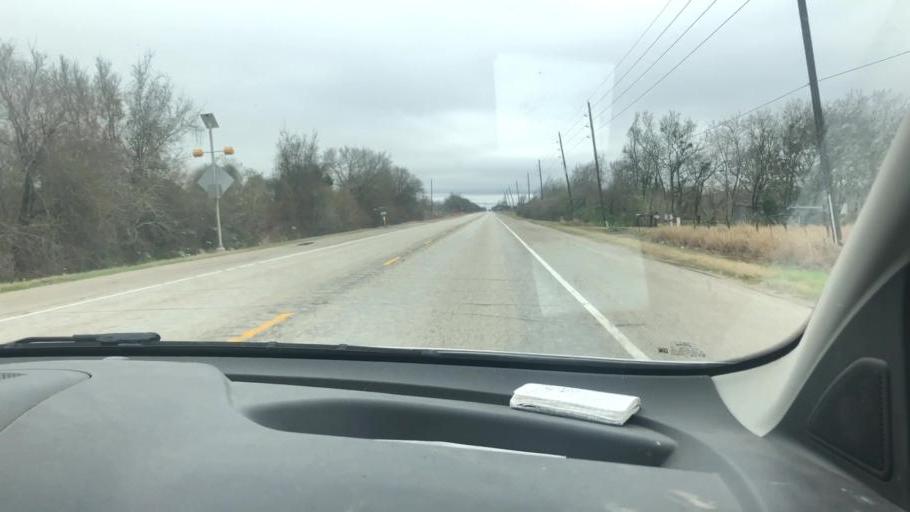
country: US
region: Texas
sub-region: Wharton County
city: Wharton
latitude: 29.2824
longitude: -96.0674
